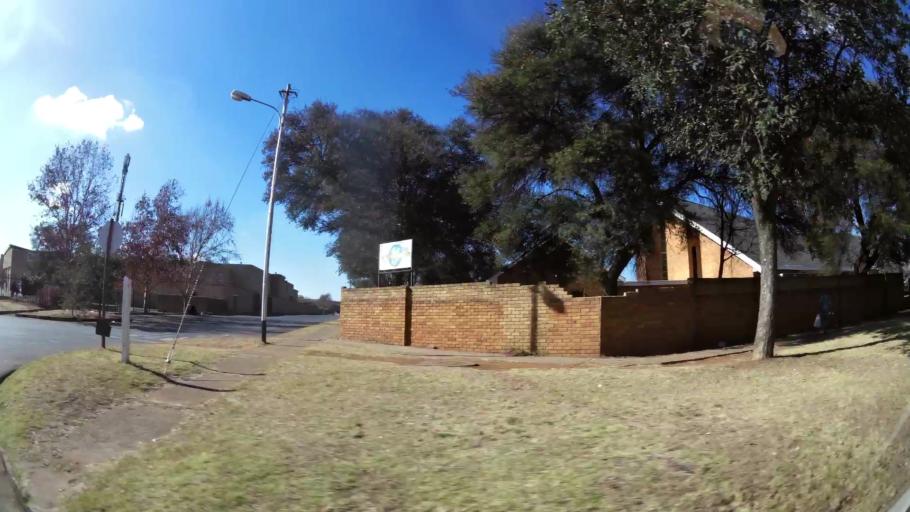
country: ZA
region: Gauteng
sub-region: City of Johannesburg Metropolitan Municipality
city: Roodepoort
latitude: -26.1414
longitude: 27.8302
